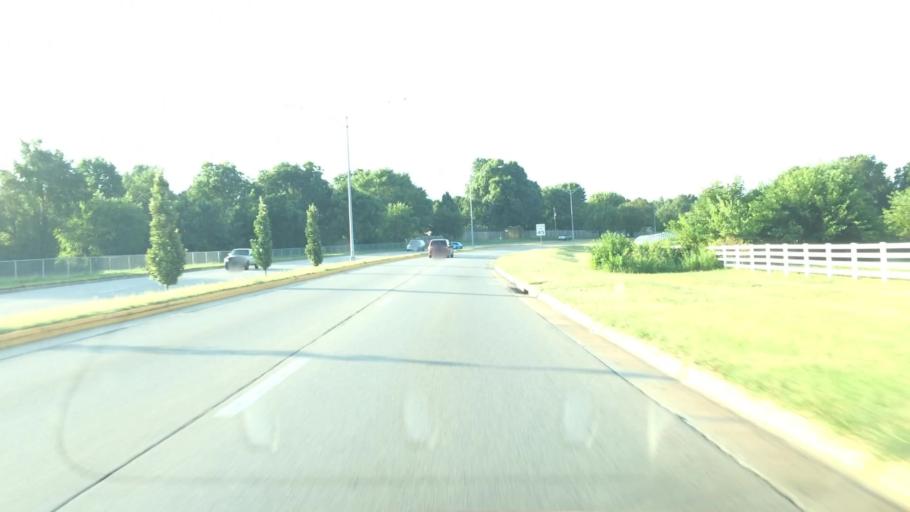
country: US
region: Missouri
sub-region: Greene County
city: Springfield
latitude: 37.1744
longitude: -93.3170
